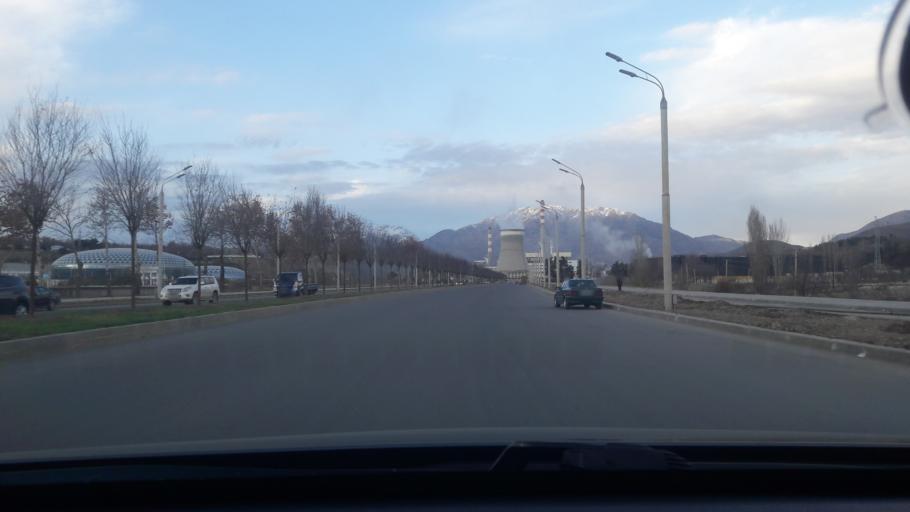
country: TJ
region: Dushanbe
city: Dushanbe
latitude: 38.5970
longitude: 68.7763
